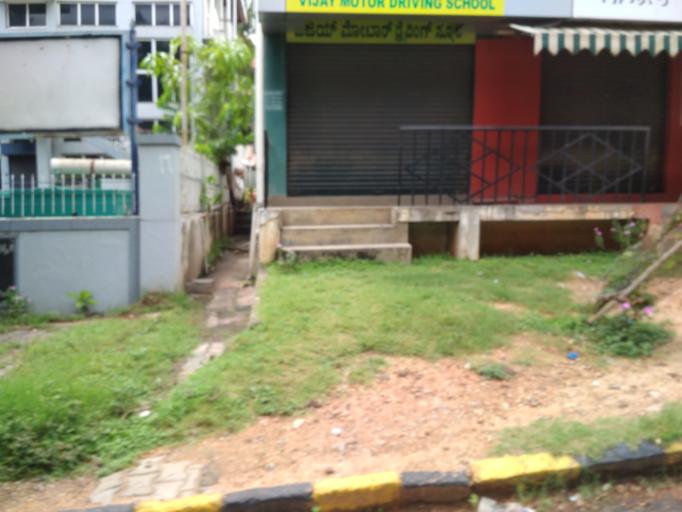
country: IN
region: Karnataka
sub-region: Mysore
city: Mysore
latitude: 12.3282
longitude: 76.6287
